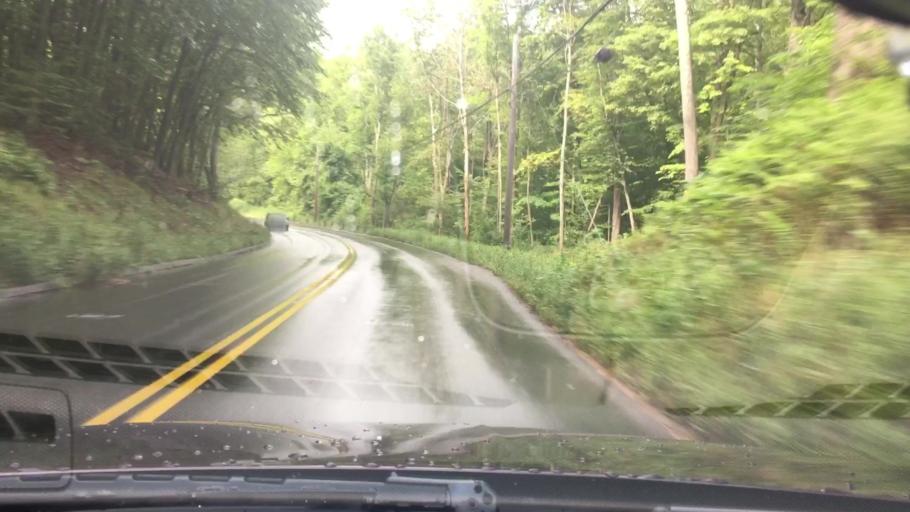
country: US
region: Connecticut
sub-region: Hartford County
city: Manchester
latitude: 41.7295
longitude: -72.5347
